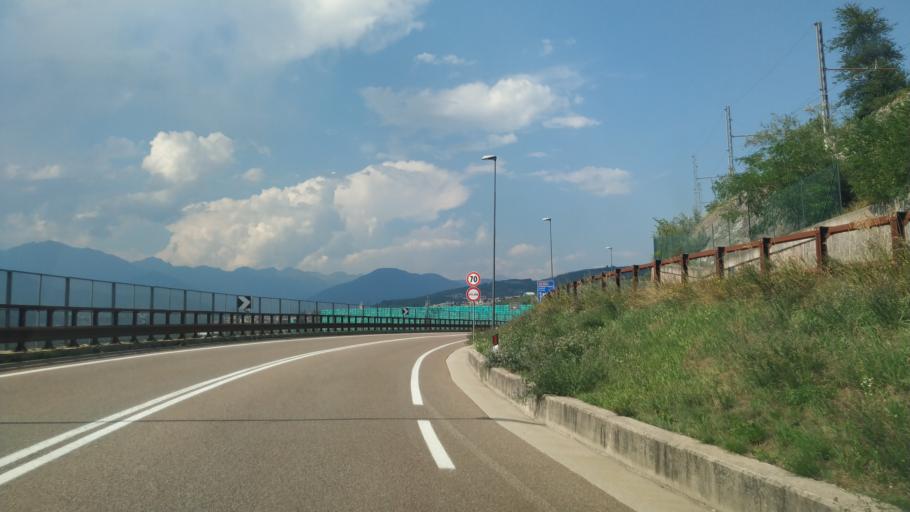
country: IT
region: Trentino-Alto Adige
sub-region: Provincia di Trento
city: Taio
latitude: 46.3076
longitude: 11.0691
